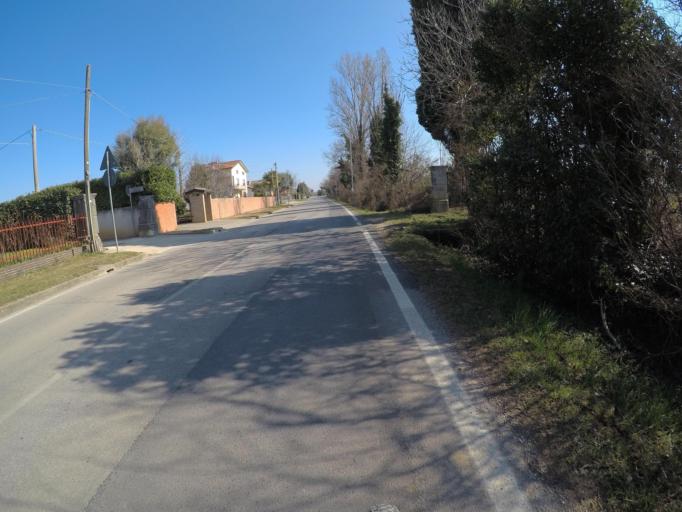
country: IT
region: Friuli Venezia Giulia
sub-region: Provincia di Udine
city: Lestizza
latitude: 45.9552
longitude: 13.1449
